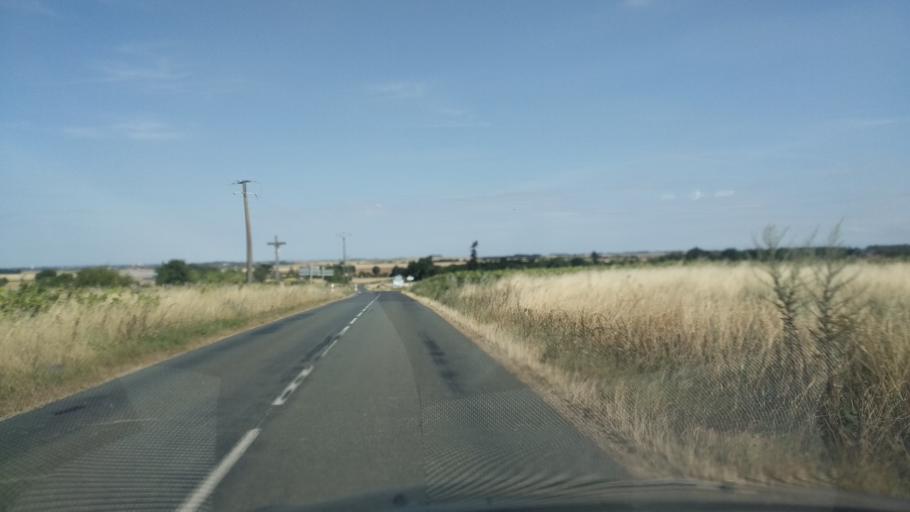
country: FR
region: Poitou-Charentes
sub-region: Departement de la Vienne
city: Vouille
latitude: 46.6825
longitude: 0.1692
